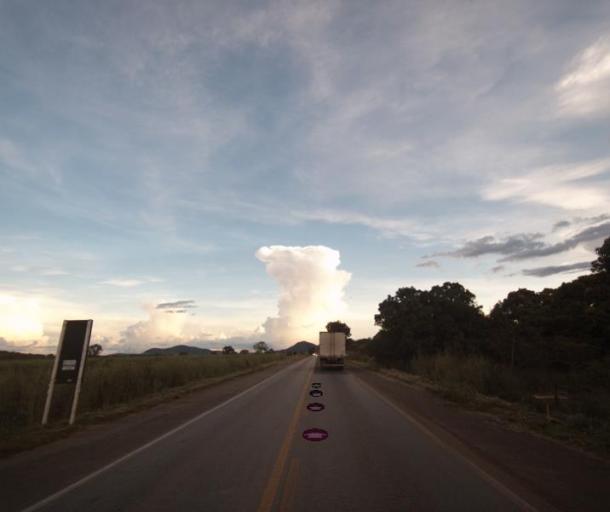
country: BR
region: Goias
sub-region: Uruacu
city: Uruacu
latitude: -14.3352
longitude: -49.1547
